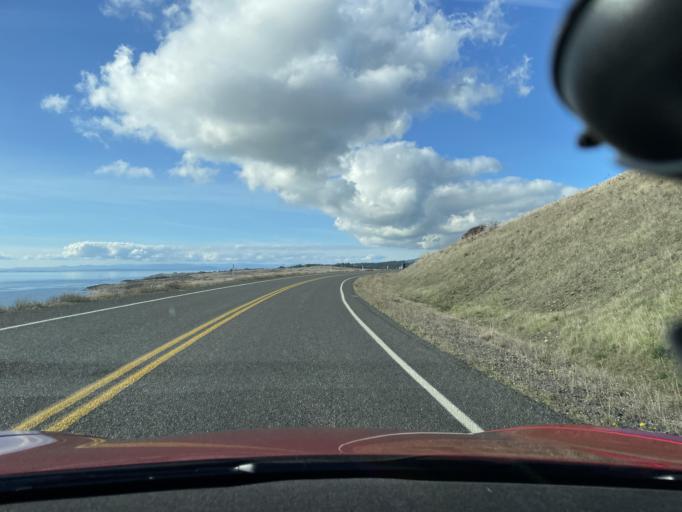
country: US
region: Washington
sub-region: San Juan County
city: Friday Harbor
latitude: 48.4566
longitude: -122.9904
